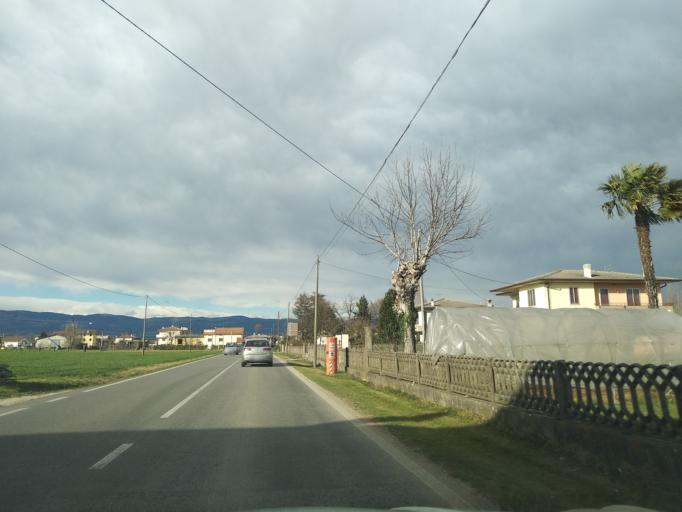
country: IT
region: Veneto
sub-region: Provincia di Vicenza
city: Poianella
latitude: 45.6258
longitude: 11.6229
